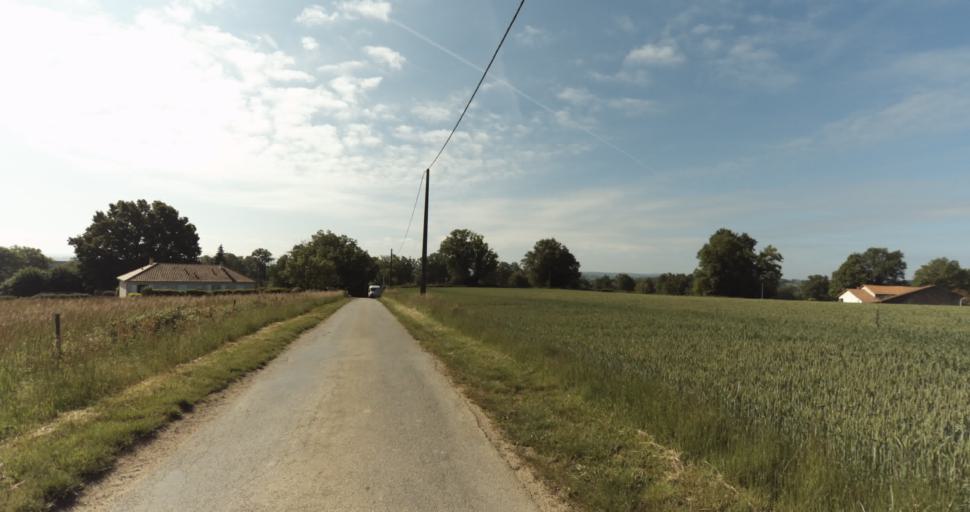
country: FR
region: Limousin
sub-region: Departement de la Haute-Vienne
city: Solignac
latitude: 45.7054
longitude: 1.2609
